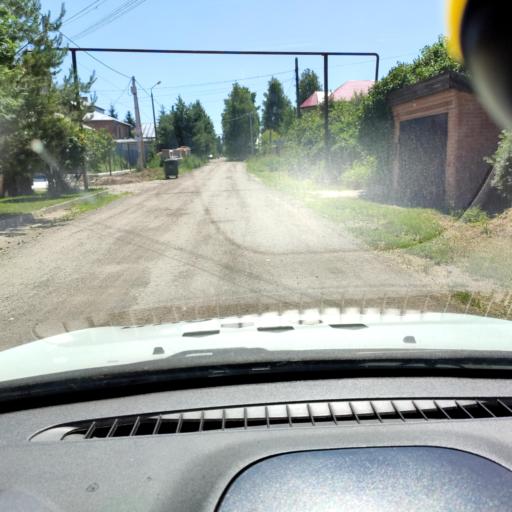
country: RU
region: Samara
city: Tol'yatti
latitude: 53.5671
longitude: 49.3864
